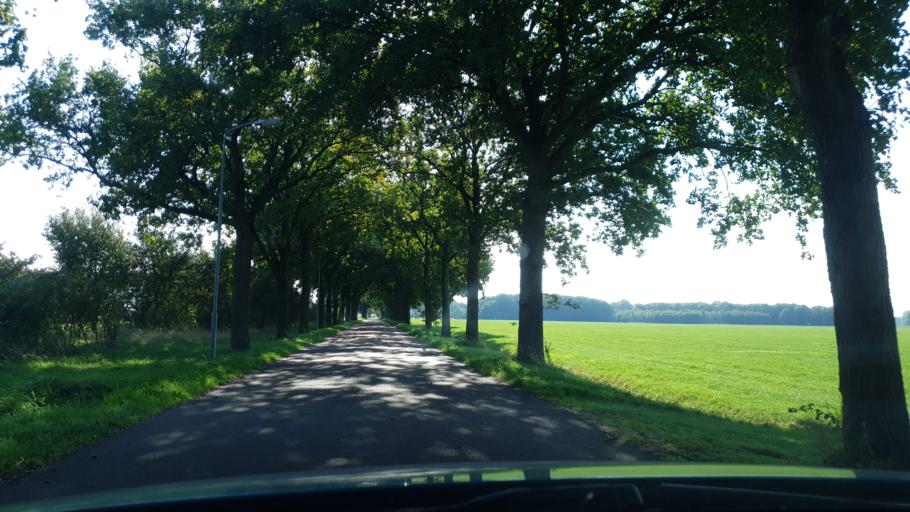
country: NL
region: Gelderland
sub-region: Gemeente Wijchen
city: Wijchen
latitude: 51.8335
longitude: 5.7455
